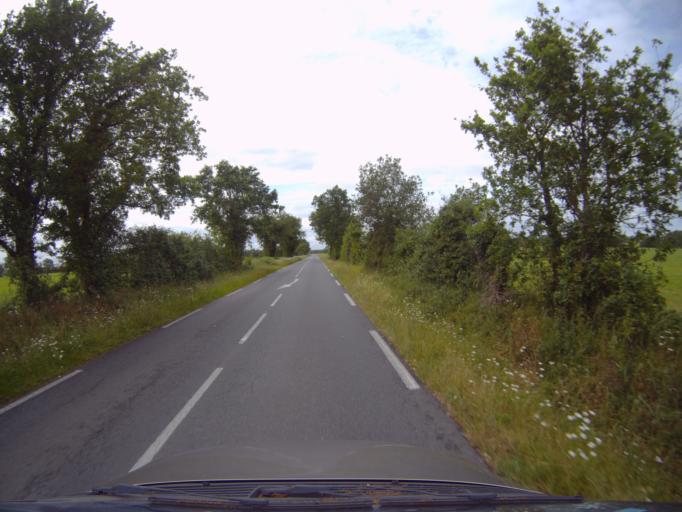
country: FR
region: Pays de la Loire
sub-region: Departement de la Loire-Atlantique
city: Montbert
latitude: 47.0597
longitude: -1.4527
